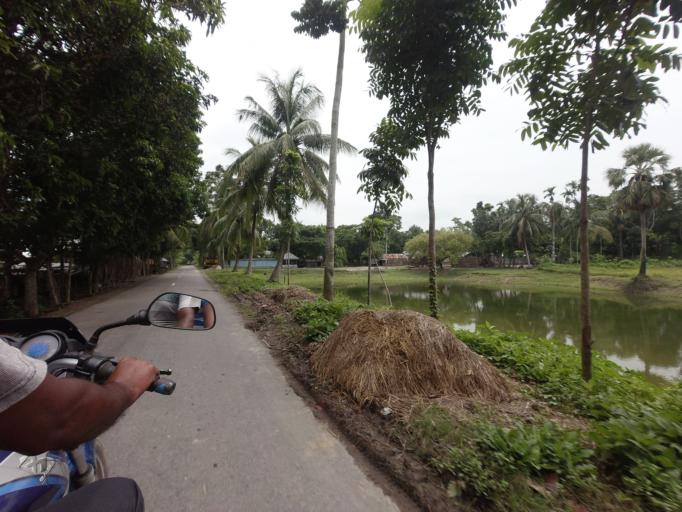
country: BD
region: Khulna
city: Kalia
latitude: 23.1005
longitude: 89.6489
